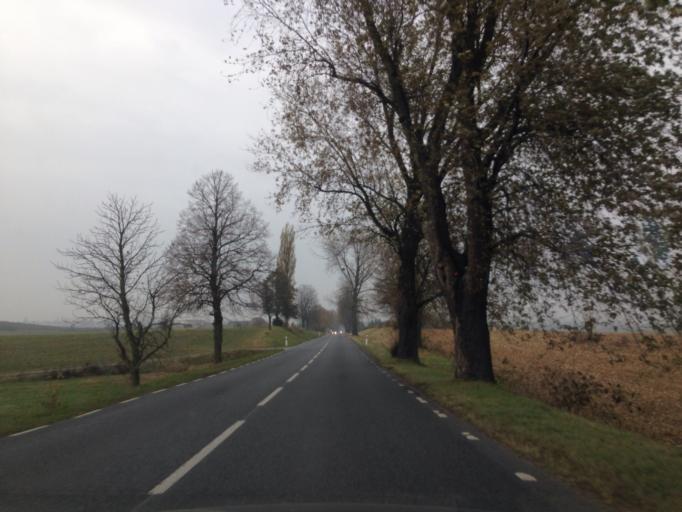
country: PL
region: Kujawsko-Pomorskie
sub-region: Powiat wabrzeski
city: Ksiazki
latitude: 53.3812
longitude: 19.0210
